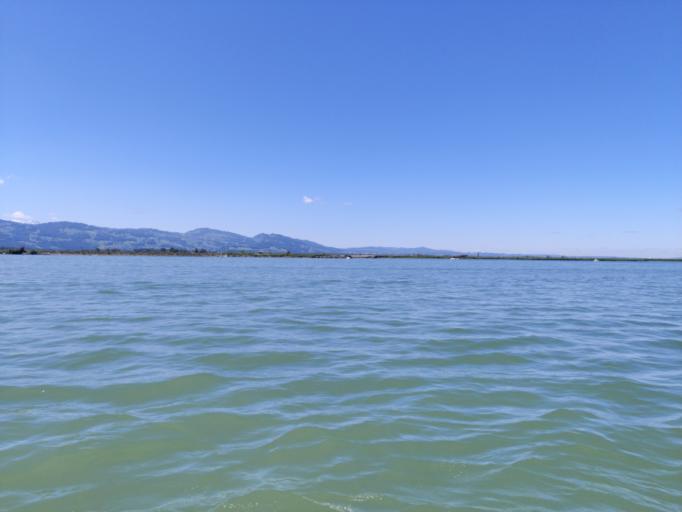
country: DE
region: Bavaria
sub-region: Swabia
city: Lindau
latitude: 47.5187
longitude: 9.6634
